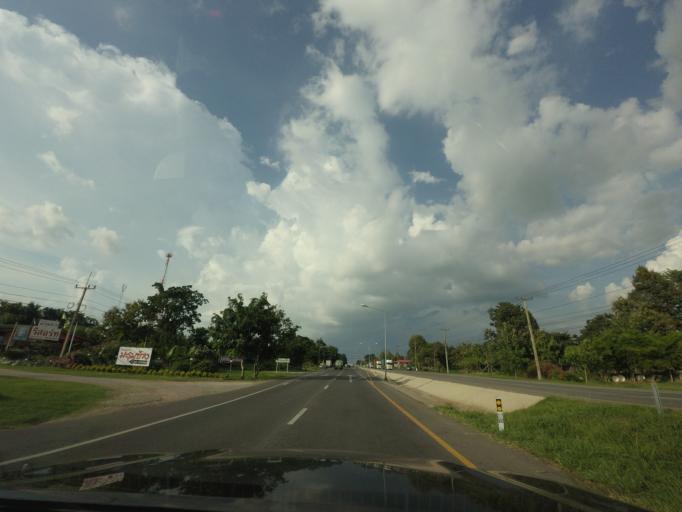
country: TH
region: Khon Kaen
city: Ban Haet
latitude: 16.2683
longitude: 102.7802
